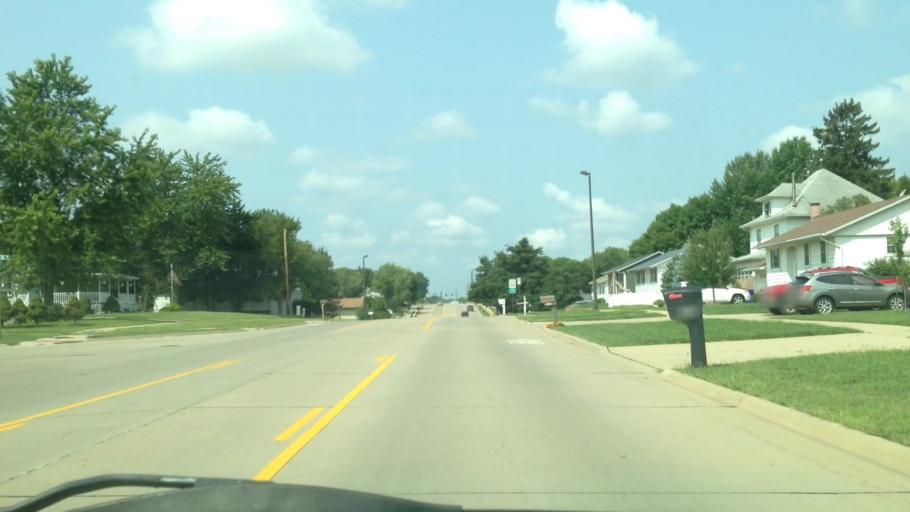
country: US
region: Iowa
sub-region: Linn County
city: Fairfax
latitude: 41.9456
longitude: -91.7088
